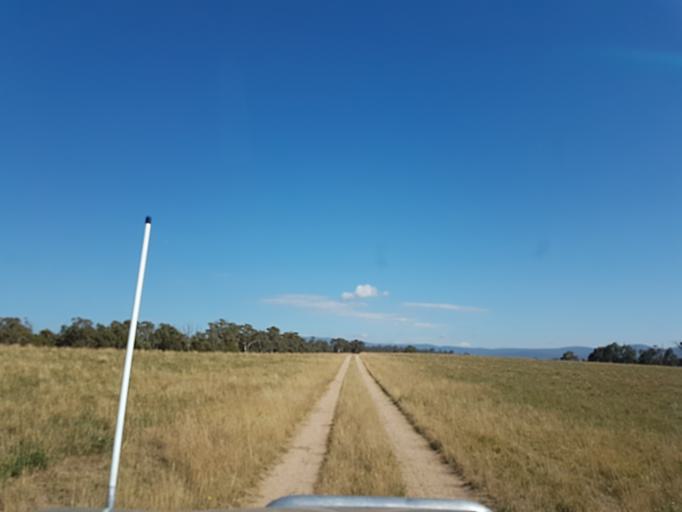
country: AU
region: New South Wales
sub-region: Snowy River
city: Jindabyne
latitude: -37.0470
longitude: 148.2881
